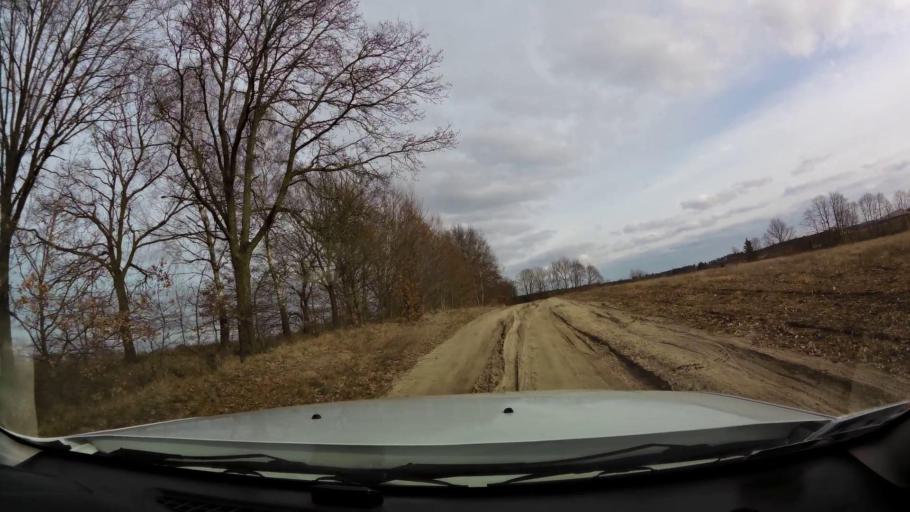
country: PL
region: West Pomeranian Voivodeship
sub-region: Powiat drawski
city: Drawsko Pomorskie
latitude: 53.5113
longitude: 15.7611
